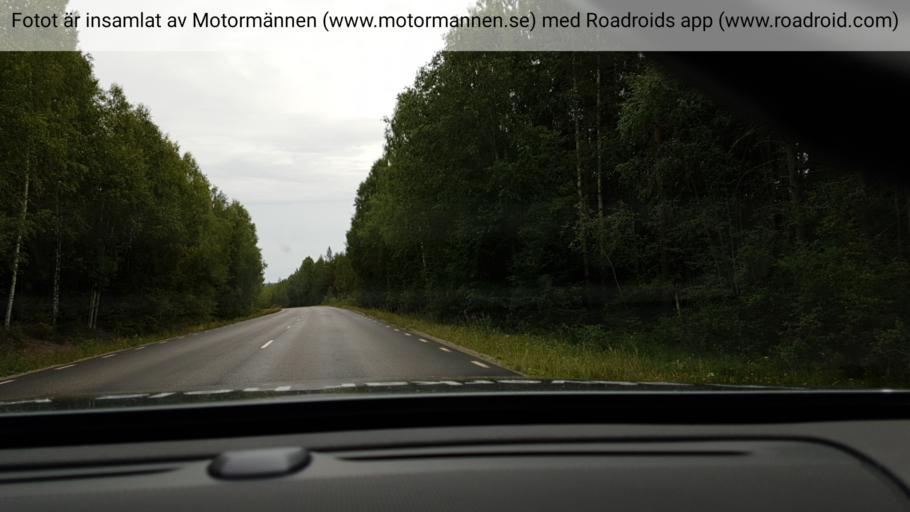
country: SE
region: Dalarna
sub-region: Ludvika Kommun
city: Ludvika
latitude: 60.2923
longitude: 15.2315
